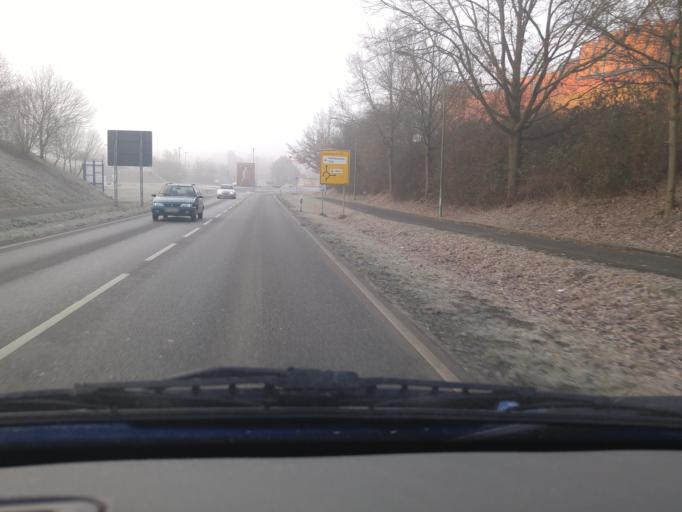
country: DE
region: Hesse
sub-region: Regierungsbezirk Darmstadt
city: Friedberg
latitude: 50.3234
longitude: 8.7479
